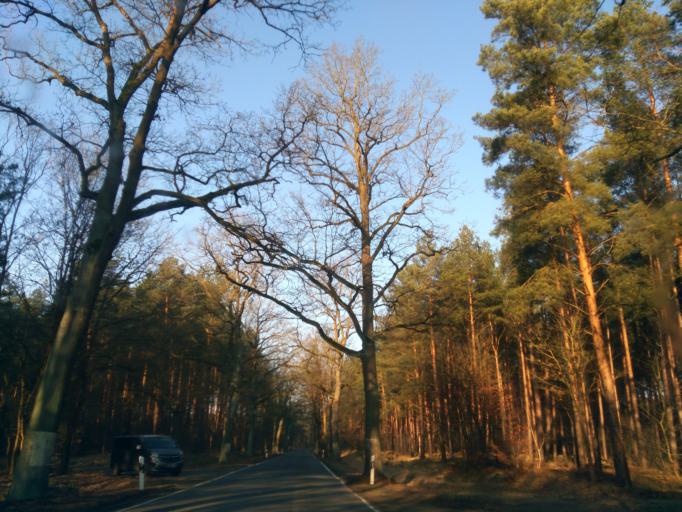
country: DE
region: Brandenburg
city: Falkensee
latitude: 52.6123
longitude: 13.1098
